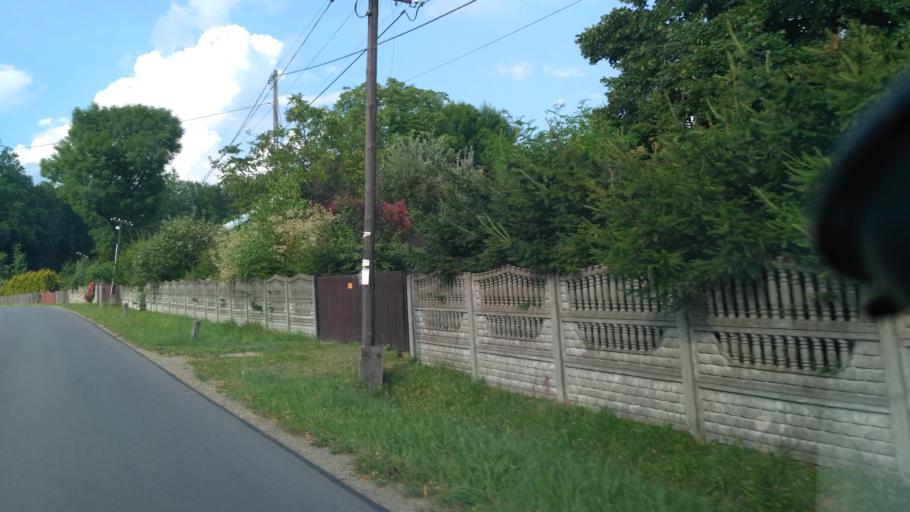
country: PL
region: Subcarpathian Voivodeship
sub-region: Powiat rzeszowski
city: Glogow Malopolski
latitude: 50.1586
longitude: 21.9818
